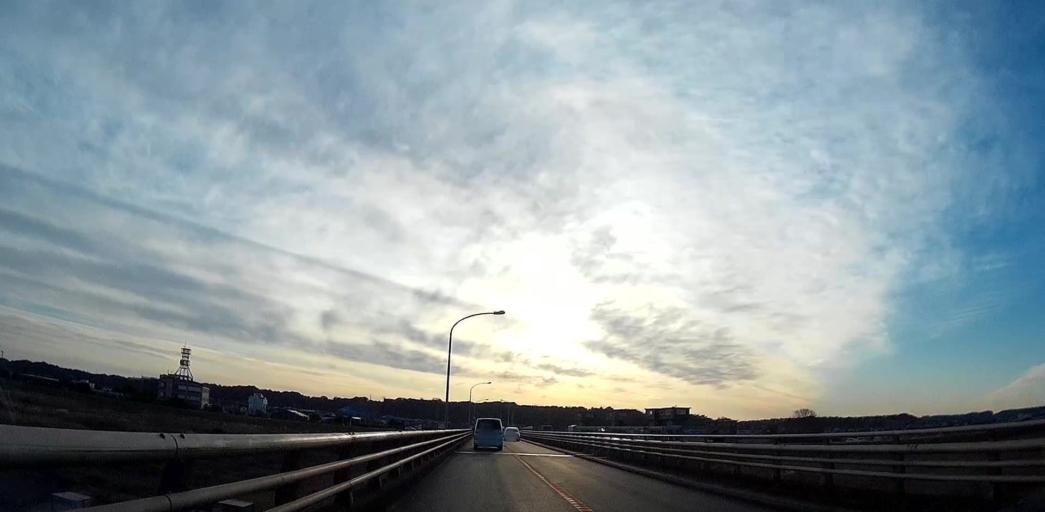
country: JP
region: Chiba
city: Omigawa
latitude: 35.8354
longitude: 140.7012
